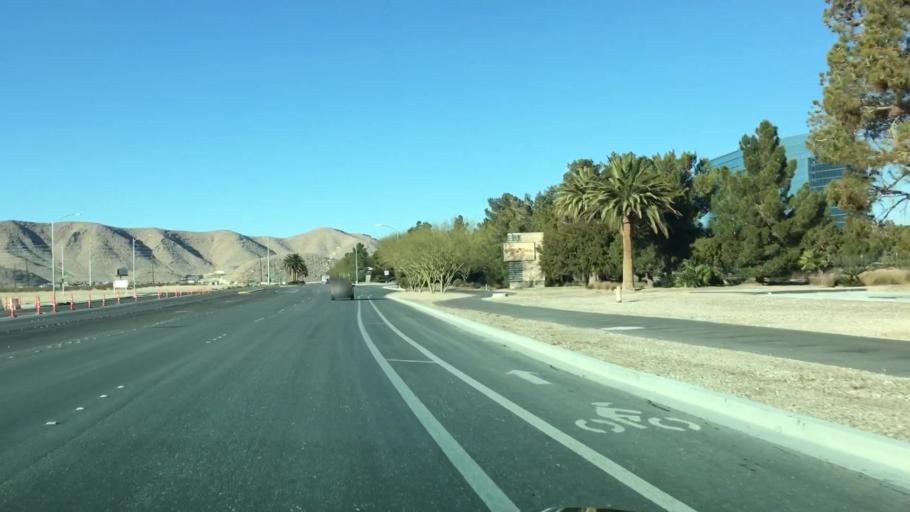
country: US
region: Nevada
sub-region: Clark County
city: Enterprise
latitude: 35.9639
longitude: -115.1657
